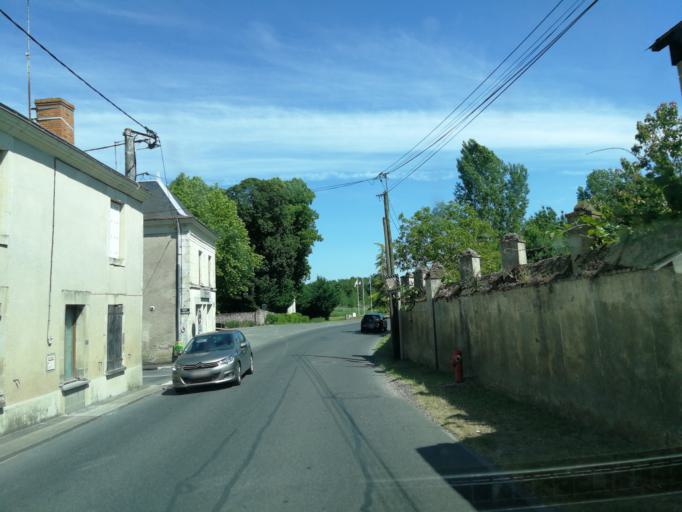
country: FR
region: Poitou-Charentes
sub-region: Departement de la Vienne
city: Moncontour
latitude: 46.9747
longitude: -0.0381
